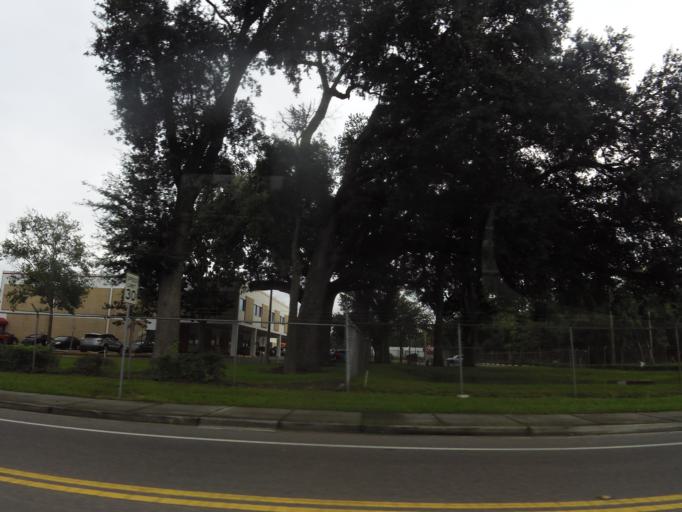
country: US
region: Florida
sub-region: Duval County
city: Jacksonville
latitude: 30.3439
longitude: -81.7139
